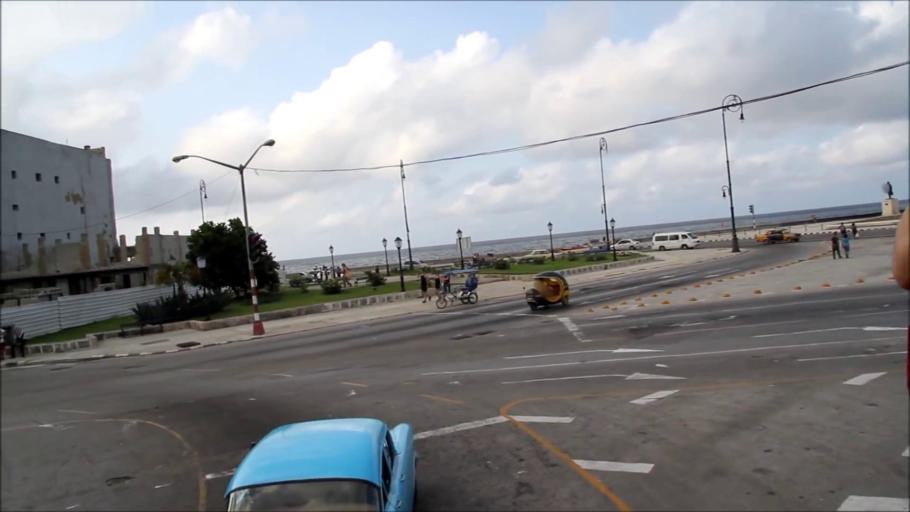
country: CU
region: La Habana
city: Centro Habana
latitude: 23.1450
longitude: -82.3583
